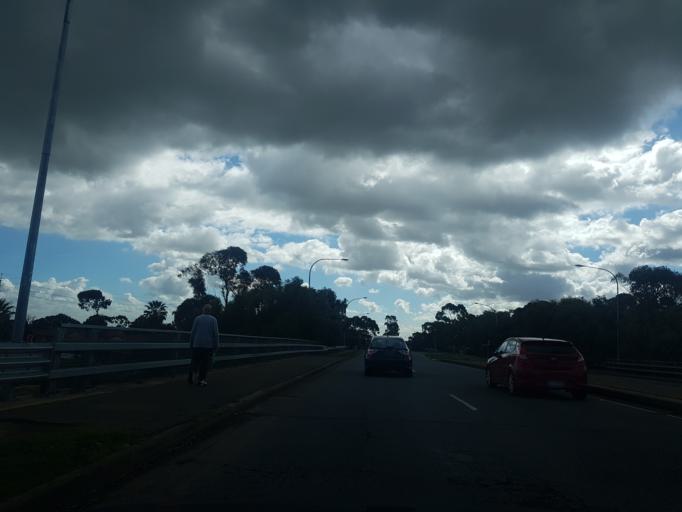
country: AU
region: South Australia
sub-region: Salisbury
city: Ingle Farm
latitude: -34.8312
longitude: 138.6458
